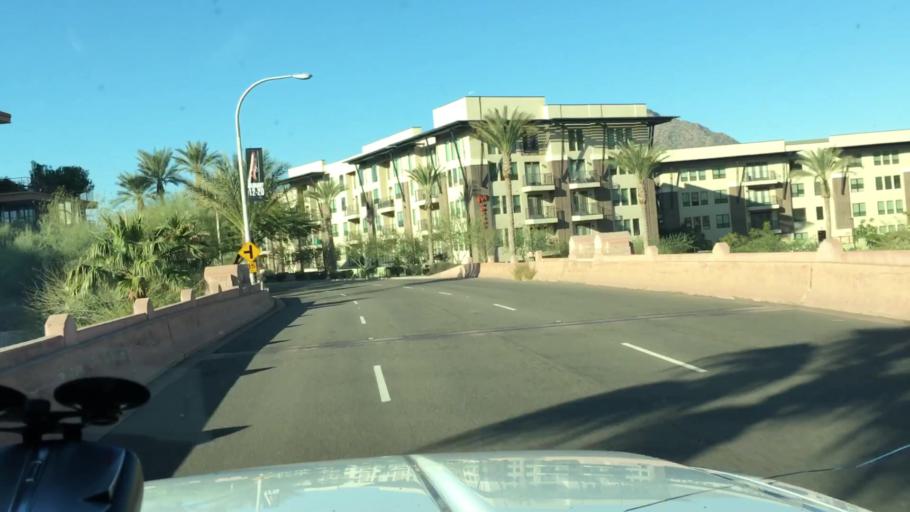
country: US
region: Arizona
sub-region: Maricopa County
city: Paradise Valley
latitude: 33.5076
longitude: -111.9281
